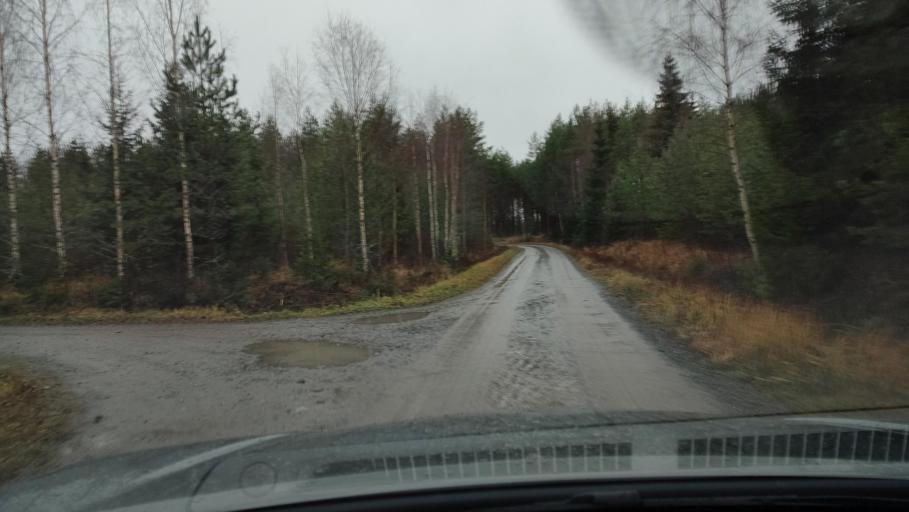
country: FI
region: Ostrobothnia
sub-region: Sydosterbotten
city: Kristinestad
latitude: 62.2337
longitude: 21.5469
